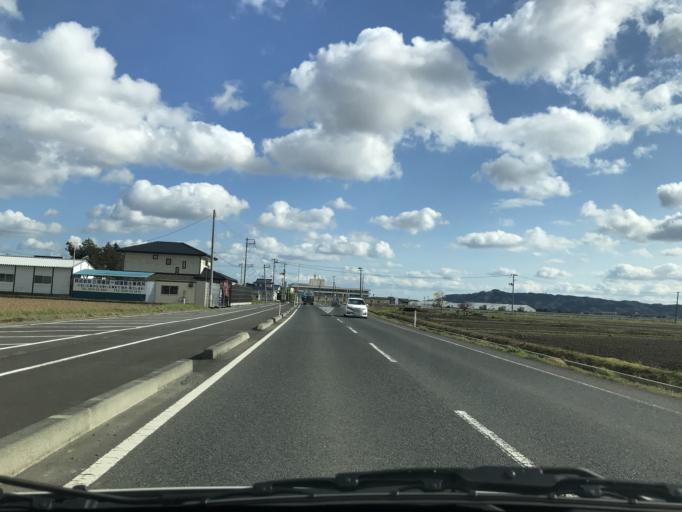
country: JP
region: Miyagi
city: Wakuya
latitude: 38.6335
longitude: 141.1880
